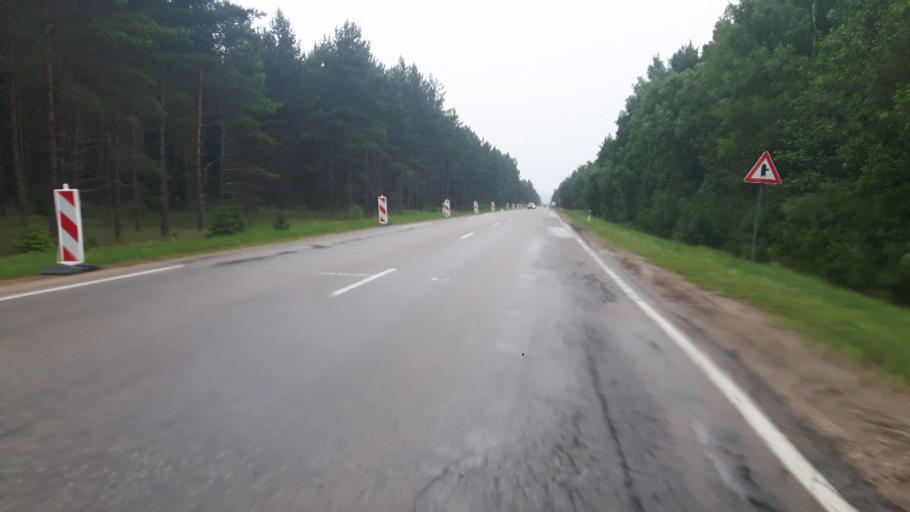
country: LV
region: Rucavas
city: Rucava
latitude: 56.1439
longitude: 21.1512
